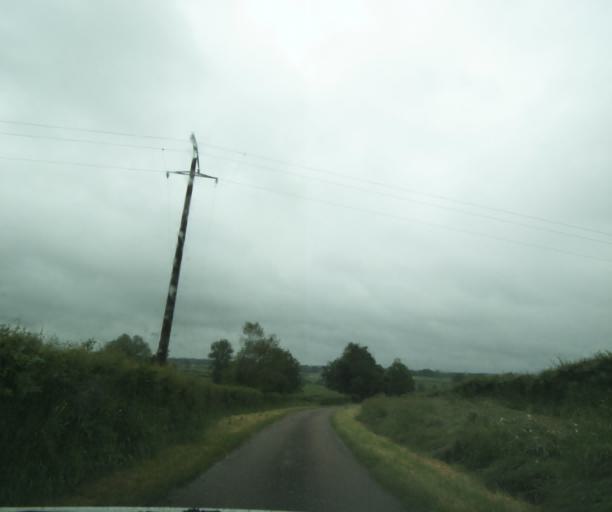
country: FR
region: Bourgogne
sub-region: Departement de Saone-et-Loire
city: Palinges
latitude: 46.4933
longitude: 4.1945
